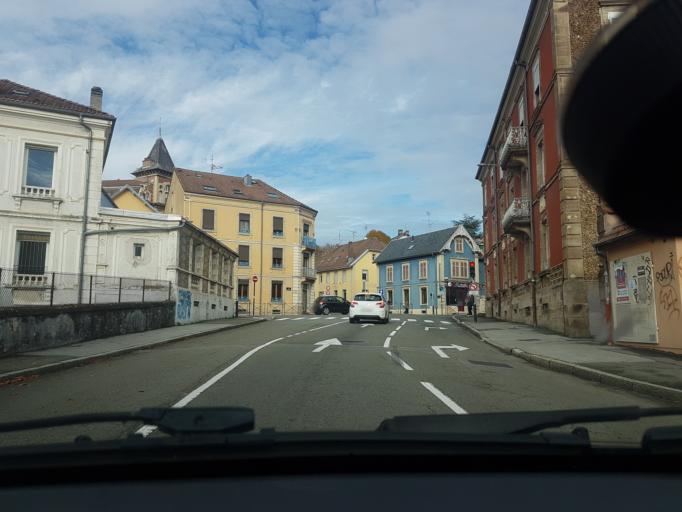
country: FR
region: Franche-Comte
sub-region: Territoire de Belfort
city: Belfort
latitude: 47.6347
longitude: 6.8520
